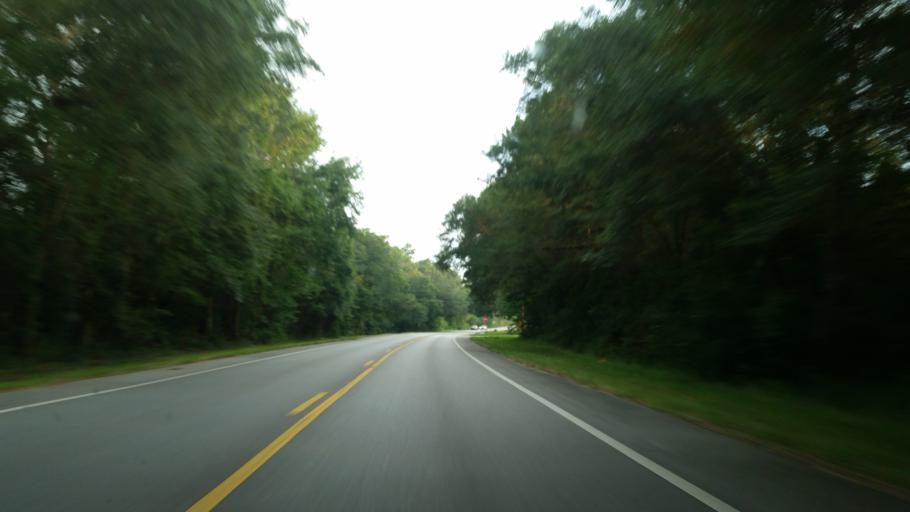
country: US
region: Florida
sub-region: Escambia County
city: Cantonment
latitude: 30.5632
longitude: -87.3448
